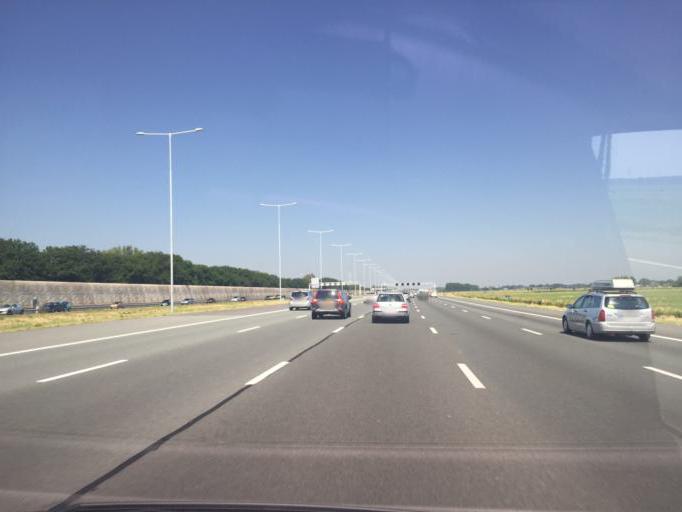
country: NL
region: Utrecht
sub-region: Stichtse Vecht
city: Vreeland
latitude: 52.2350
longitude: 4.9773
